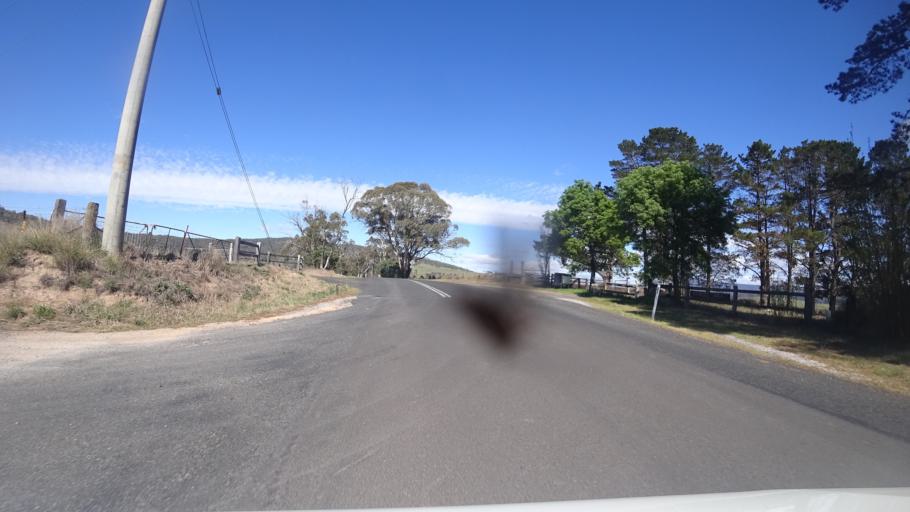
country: AU
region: New South Wales
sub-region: Lithgow
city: Bowenfels
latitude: -33.5177
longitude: 149.9885
